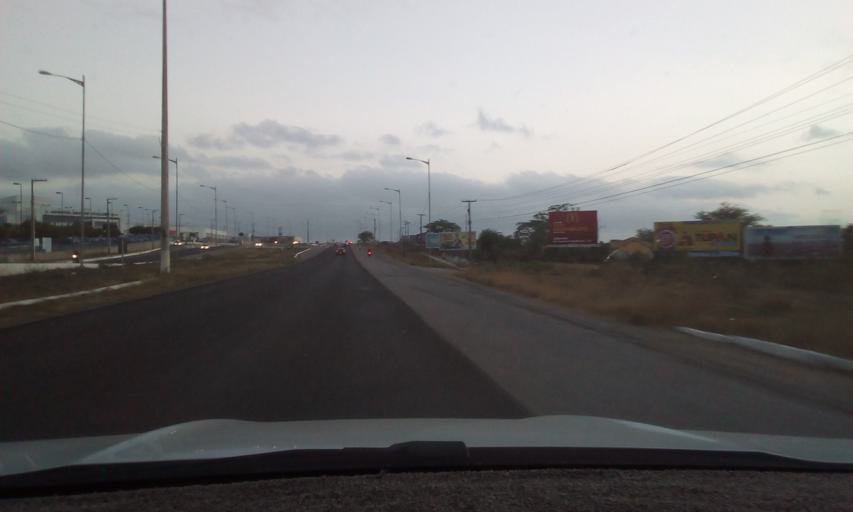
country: BR
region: Pernambuco
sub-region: Caruaru
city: Caruaru
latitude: -8.2432
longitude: -35.9754
